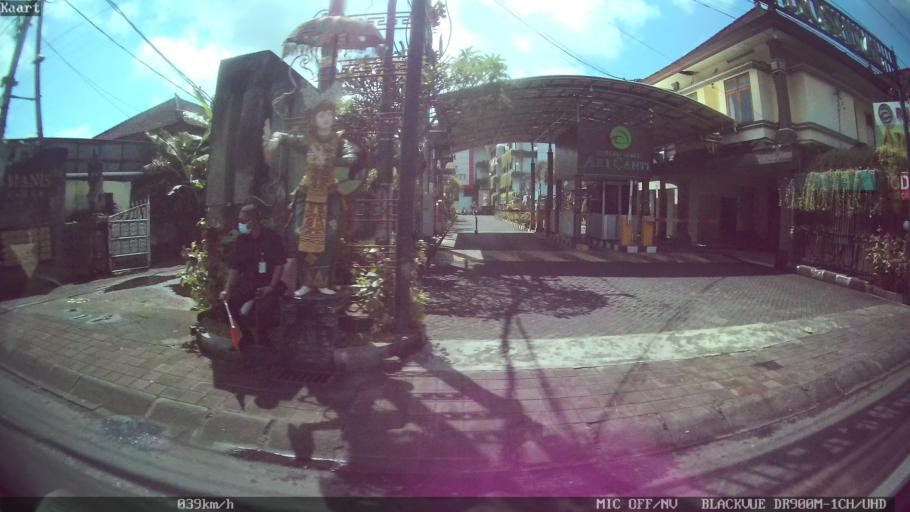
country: ID
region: Bali
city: Banjar Tebongkang
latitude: -8.5517
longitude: 115.2725
